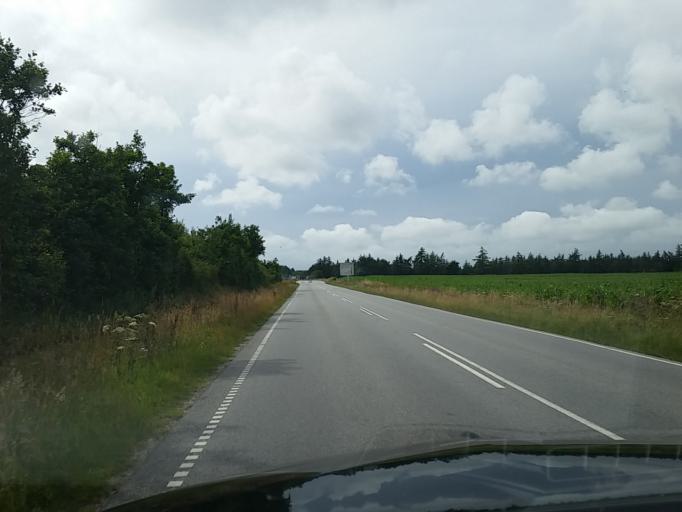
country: DK
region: South Denmark
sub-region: Varde Kommune
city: Oksbol
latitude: 55.7874
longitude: 8.2550
